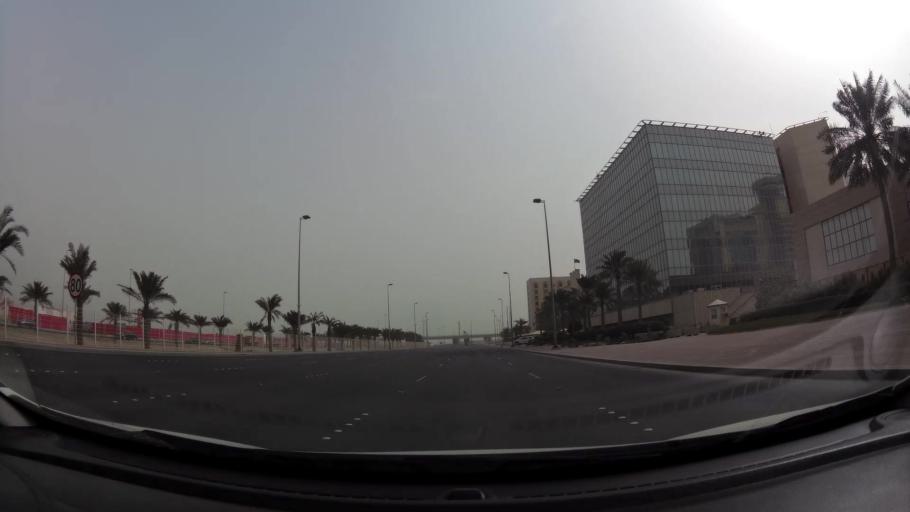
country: BH
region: Manama
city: Manama
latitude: 26.2431
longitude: 50.5861
